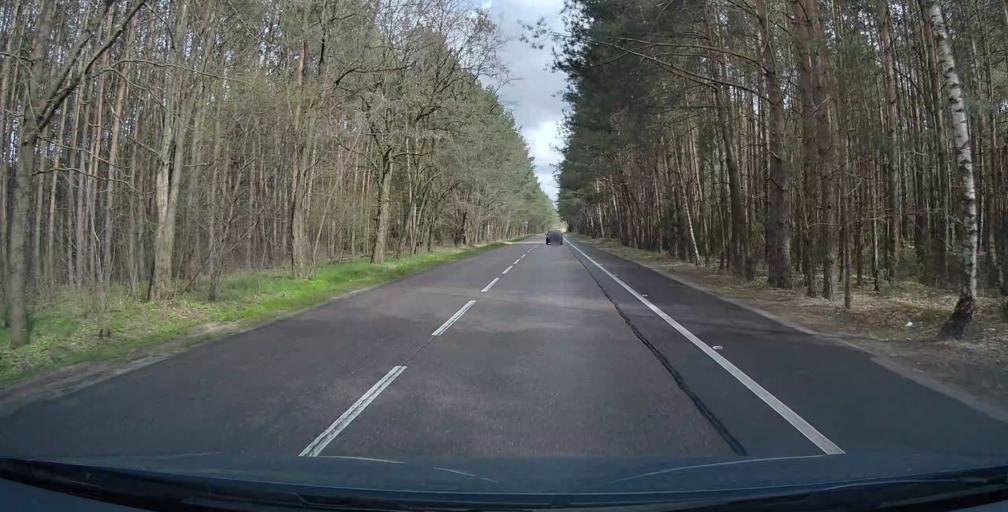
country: PL
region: Masovian Voivodeship
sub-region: Powiat wyszkowski
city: Dlugosiodlo
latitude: 52.7754
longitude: 21.5497
